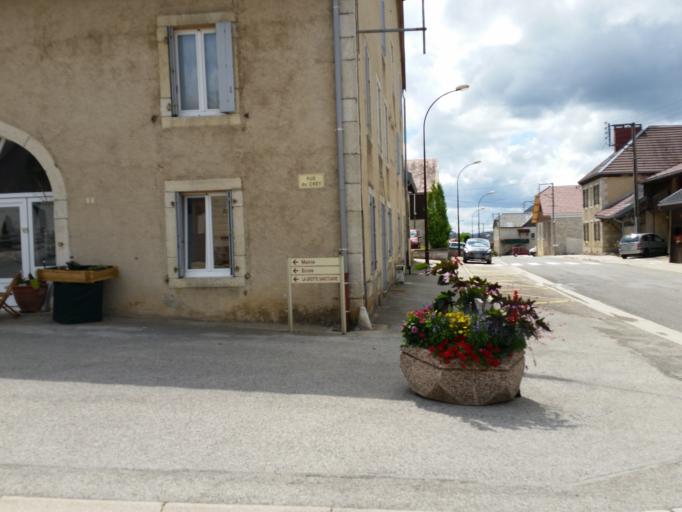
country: FR
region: Franche-Comte
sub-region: Departement du Doubs
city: Jougne
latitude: 46.7543
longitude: 6.3170
